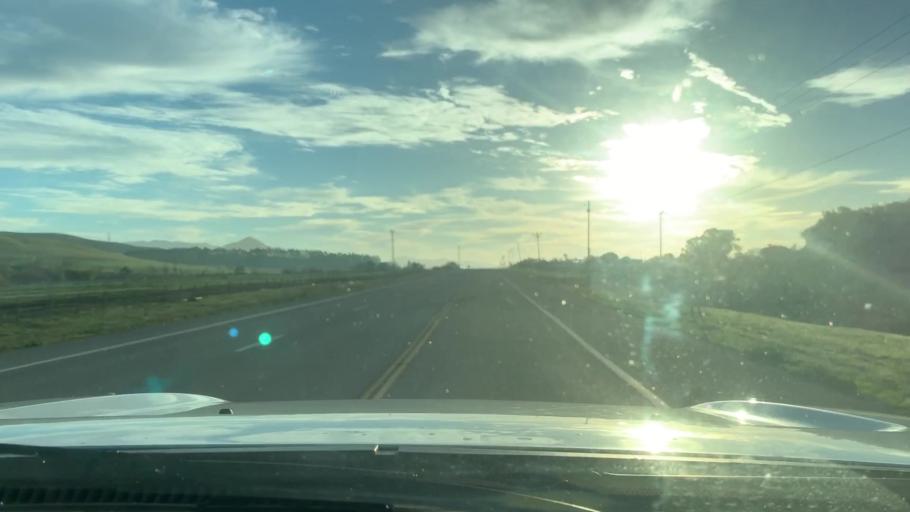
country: US
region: California
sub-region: San Luis Obispo County
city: Los Osos
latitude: 35.2899
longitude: -120.7475
